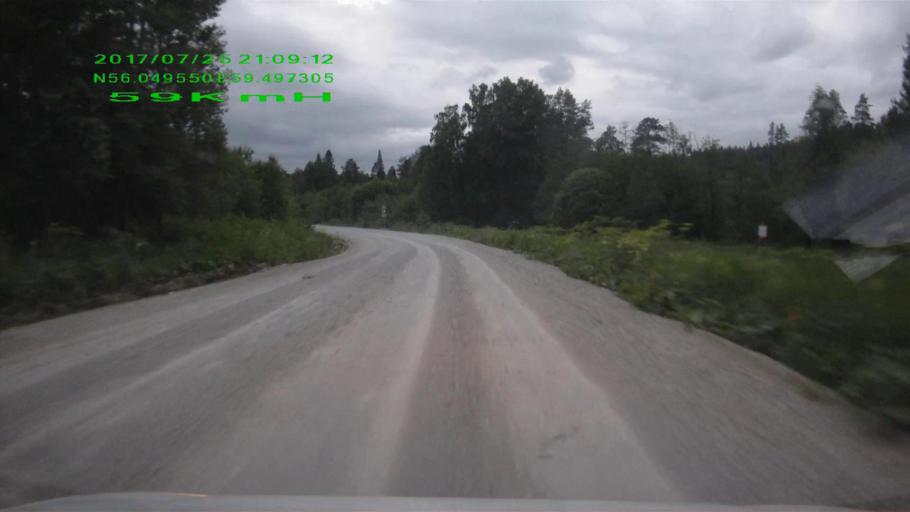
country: RU
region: Chelyabinsk
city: Nyazepetrovsk
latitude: 56.0497
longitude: 59.4968
